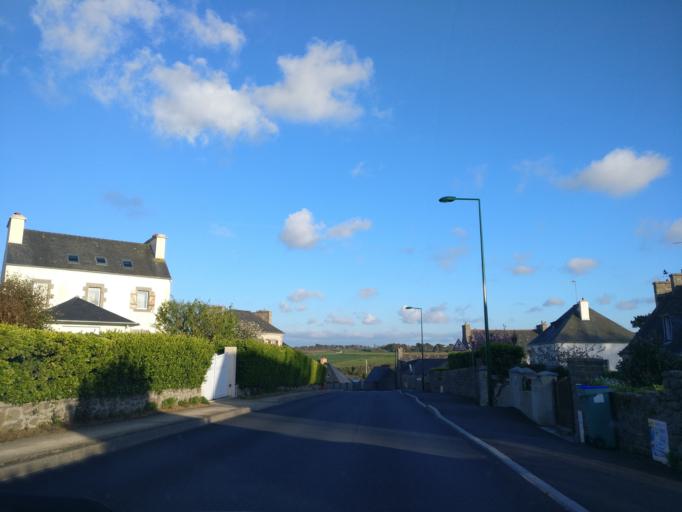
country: FR
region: Brittany
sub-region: Departement du Finistere
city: Lampaul-Plouarzel
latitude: 48.4740
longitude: -4.7559
